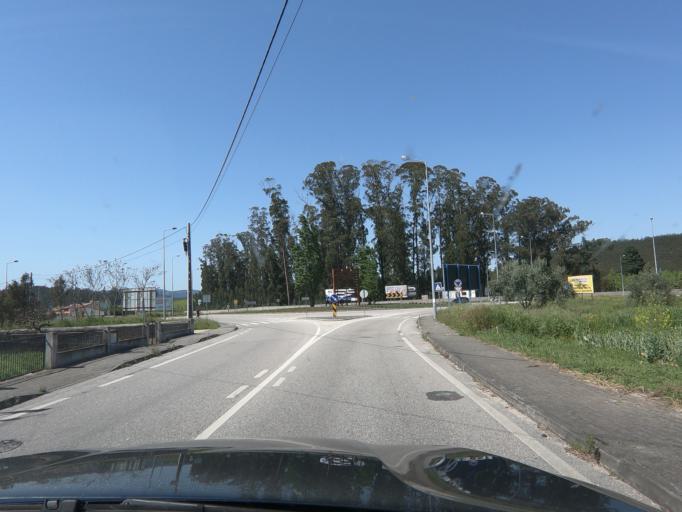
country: PT
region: Coimbra
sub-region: Lousa
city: Lousa
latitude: 40.1353
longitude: -8.2503
